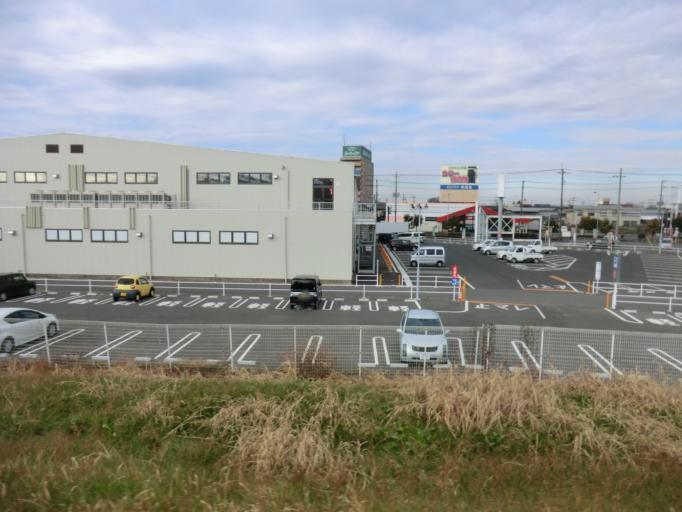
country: JP
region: Ibaraki
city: Mitsukaido
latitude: 36.0161
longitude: 139.9941
